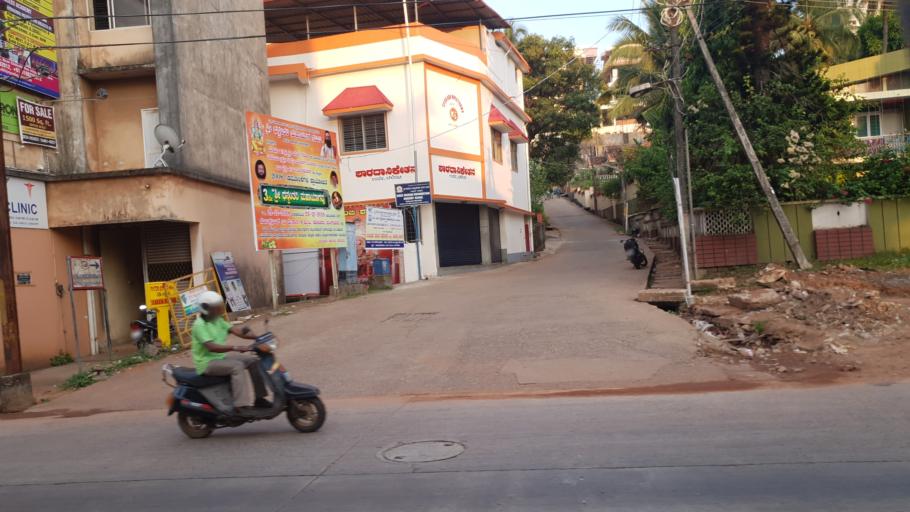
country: IN
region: Karnataka
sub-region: Dakshina Kannada
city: Mangalore
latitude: 12.8942
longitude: 74.8358
